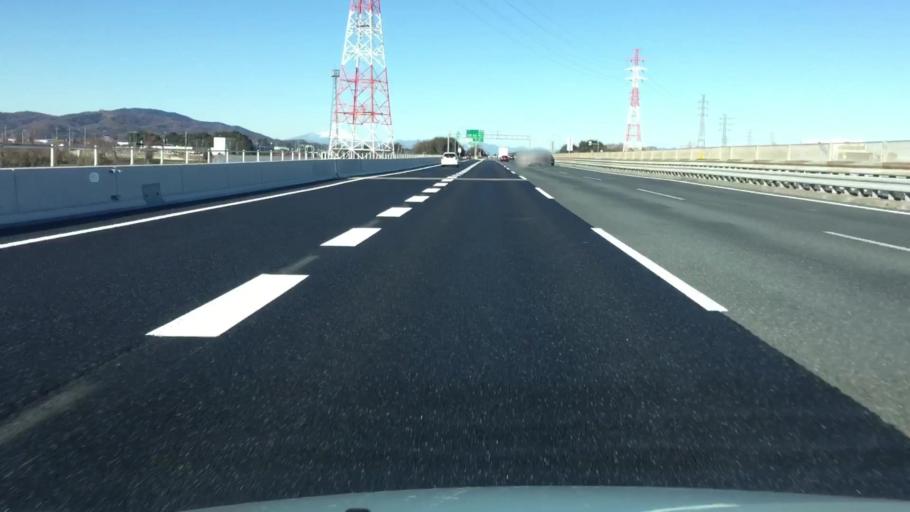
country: JP
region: Saitama
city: Yorii
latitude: 36.1213
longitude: 139.2535
